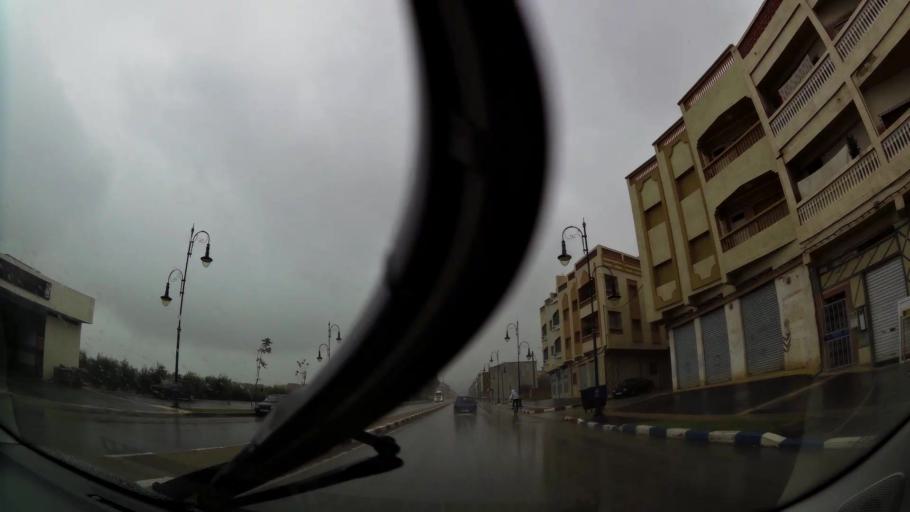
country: MA
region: Taza-Al Hoceima-Taounate
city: Imzourene
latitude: 35.1124
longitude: -3.8417
